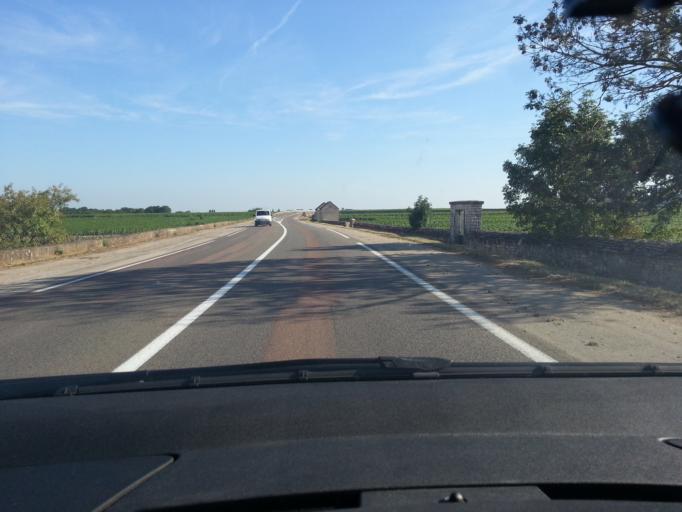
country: FR
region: Bourgogne
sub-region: Departement de la Cote-d'Or
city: Nuits-Saint-Georges
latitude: 47.1697
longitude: 4.9625
